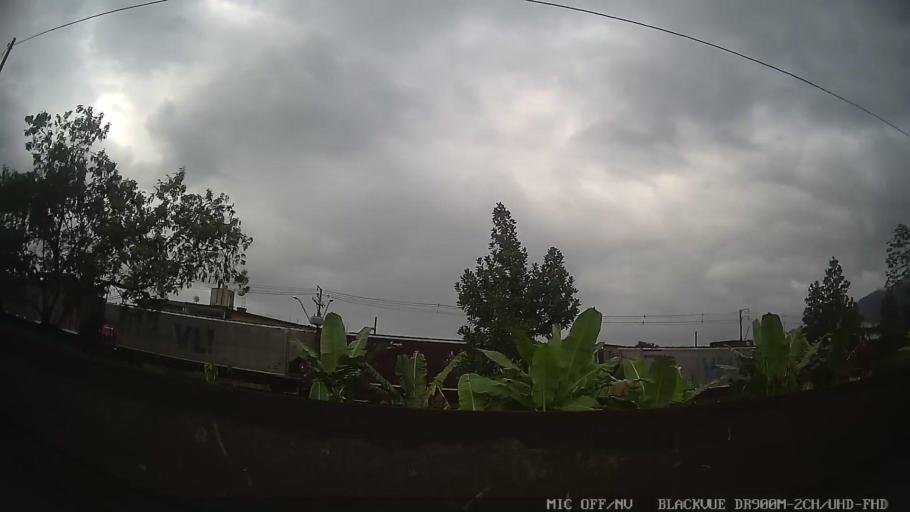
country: BR
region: Sao Paulo
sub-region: Cubatao
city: Cubatao
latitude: -23.8995
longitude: -46.4484
